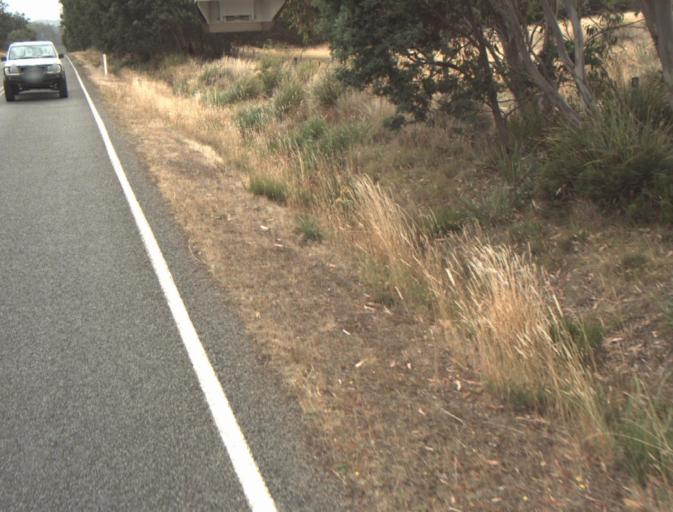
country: AU
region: Tasmania
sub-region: Northern Midlands
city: Evandale
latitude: -41.4742
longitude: 147.5422
